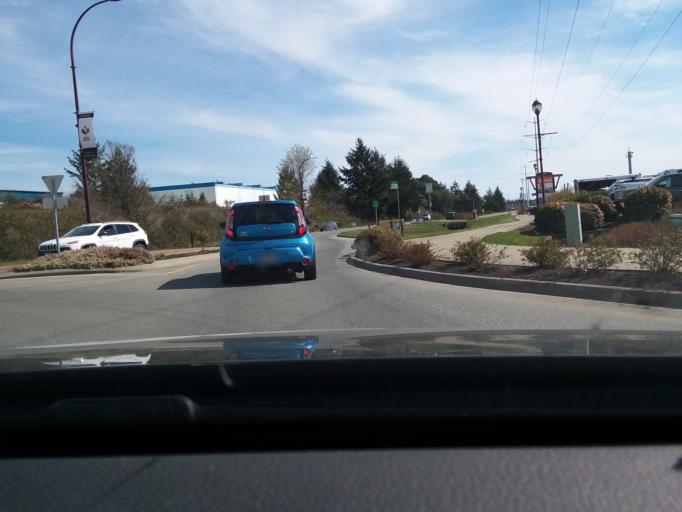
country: CA
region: British Columbia
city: Langford
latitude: 48.4434
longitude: -123.5200
